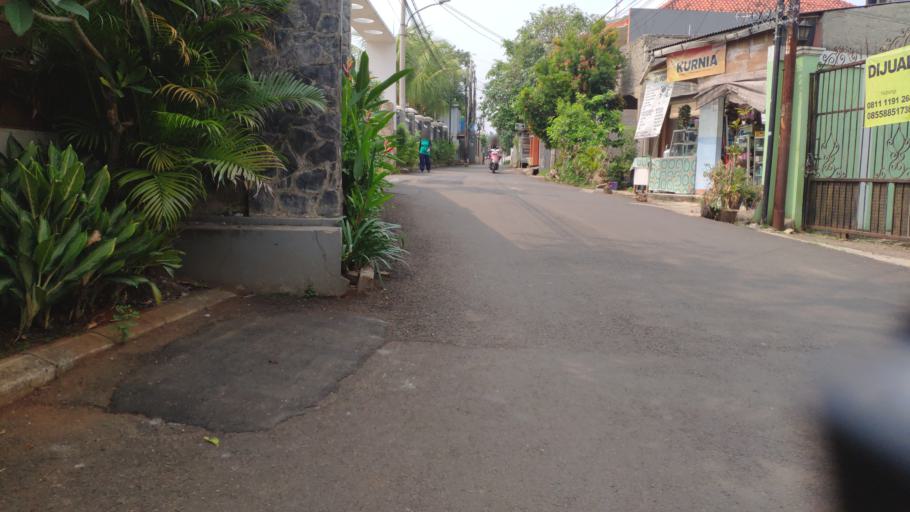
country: ID
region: West Java
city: Depok
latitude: -6.3216
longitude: 106.8215
